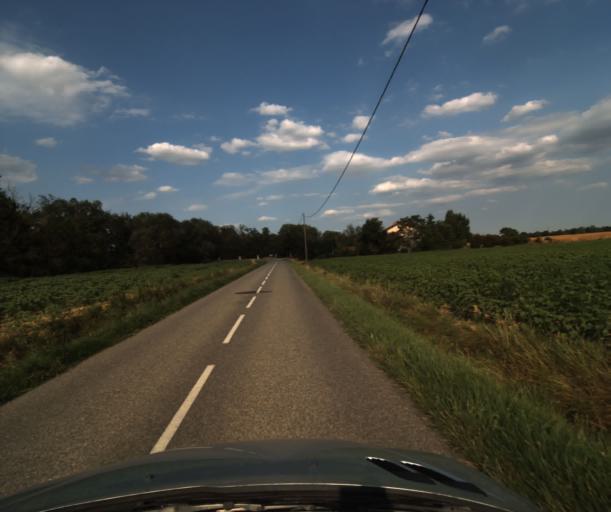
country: FR
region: Midi-Pyrenees
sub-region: Departement de la Haute-Garonne
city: Fonsorbes
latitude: 43.5161
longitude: 1.2265
